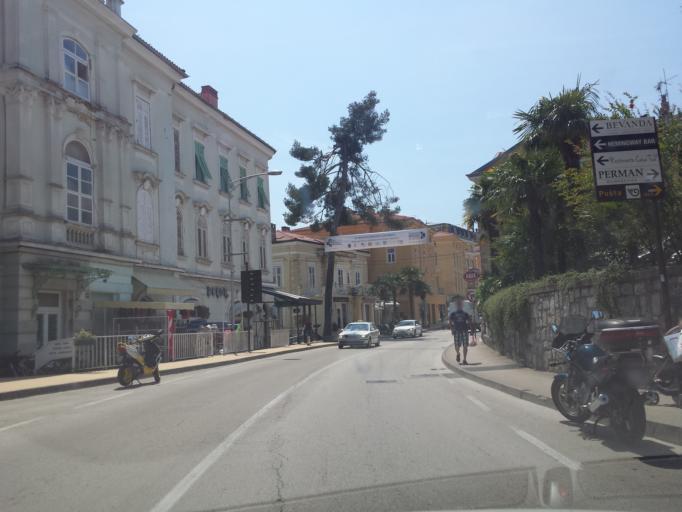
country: HR
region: Primorsko-Goranska
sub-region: Grad Opatija
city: Opatija
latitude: 45.3392
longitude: 14.3095
